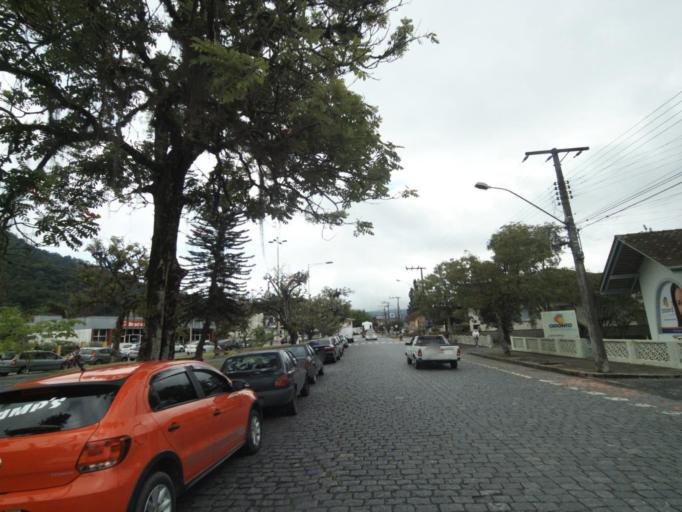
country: BR
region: Santa Catarina
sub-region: Pomerode
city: Pomerode
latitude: -26.7423
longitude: -49.1750
